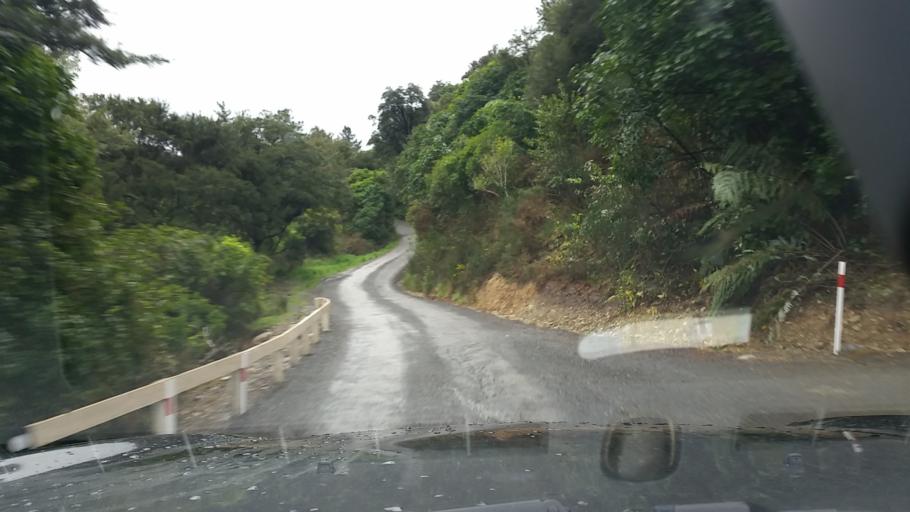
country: NZ
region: Marlborough
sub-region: Marlborough District
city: Picton
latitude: -41.2879
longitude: 174.0379
